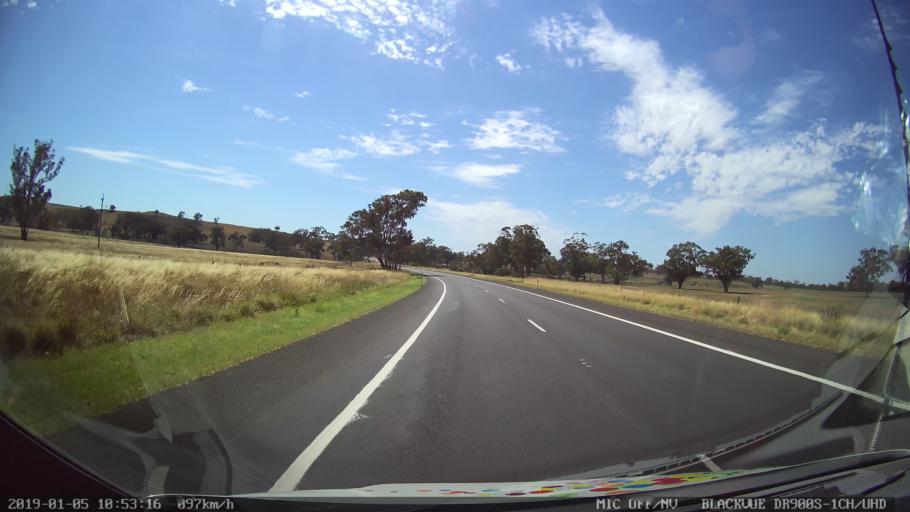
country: AU
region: New South Wales
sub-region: Warrumbungle Shire
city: Coonabarabran
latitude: -31.4415
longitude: 149.1115
